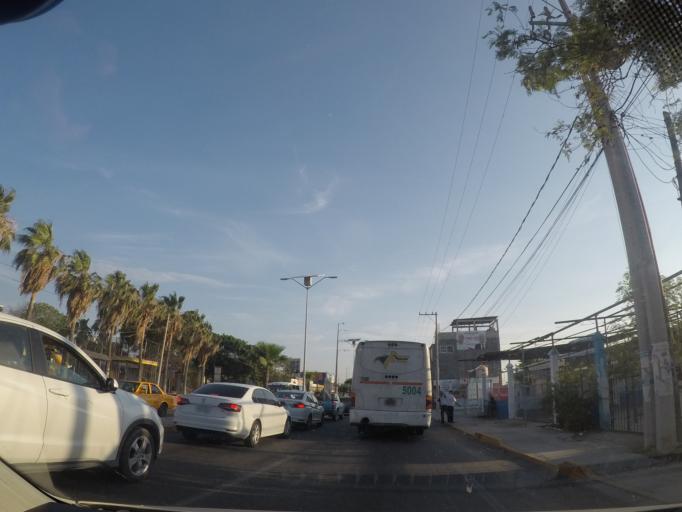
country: MX
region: Oaxaca
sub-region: Salina Cruz
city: Salina Cruz
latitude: 16.1990
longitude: -95.2020
